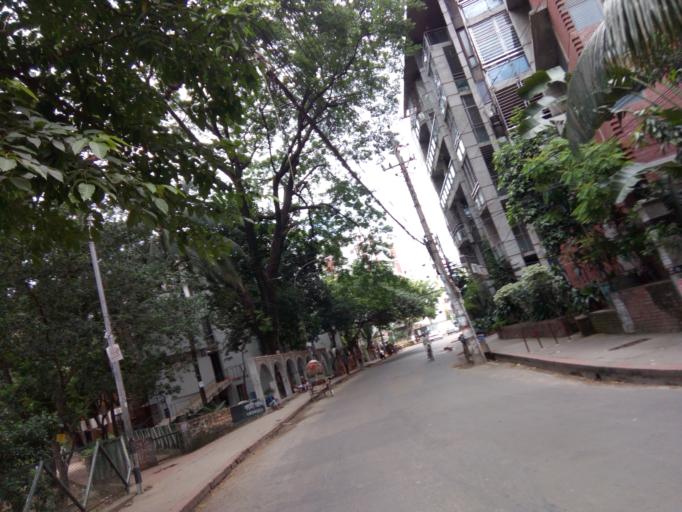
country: BD
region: Dhaka
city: Azimpur
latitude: 23.7506
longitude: 90.3739
